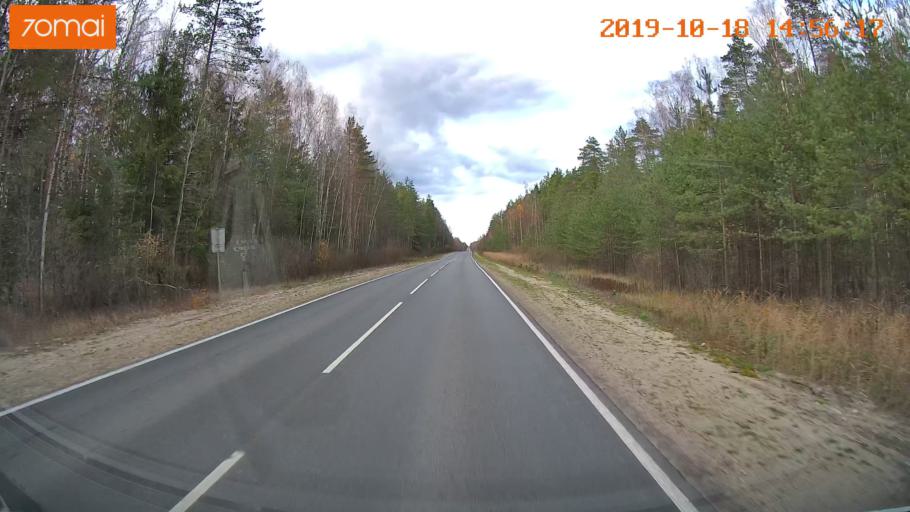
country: RU
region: Vladimir
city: Kurlovo
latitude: 55.4625
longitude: 40.5883
